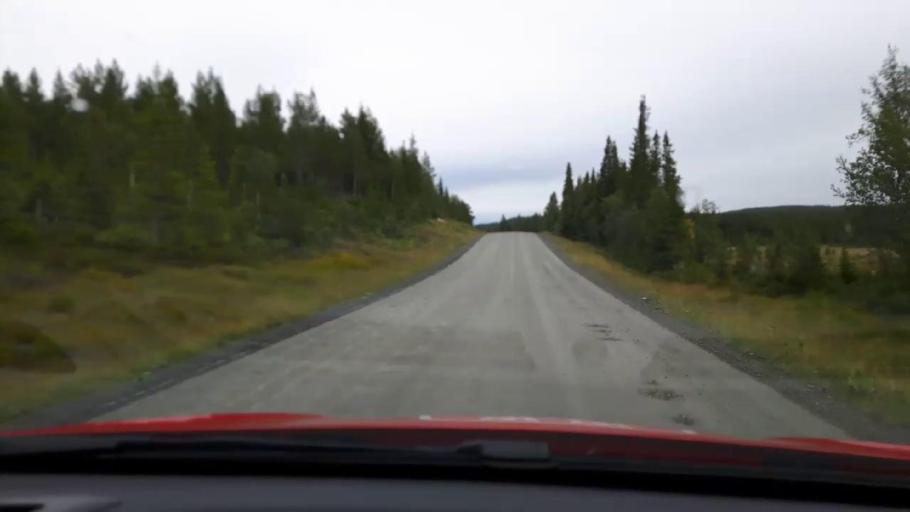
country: SE
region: Jaemtland
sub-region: Are Kommun
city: Are
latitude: 63.4356
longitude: 13.2672
